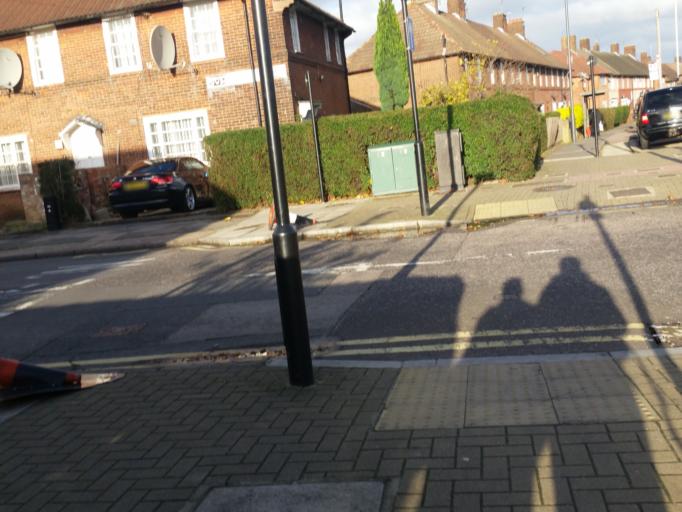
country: GB
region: England
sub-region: Greater London
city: Harringay
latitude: 51.6014
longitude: -0.0915
